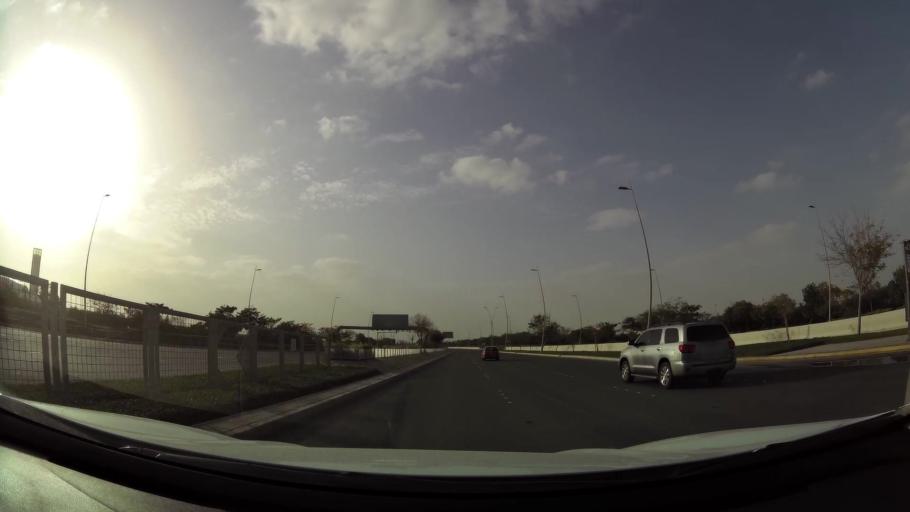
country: AE
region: Abu Dhabi
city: Abu Dhabi
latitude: 24.4965
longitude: 54.5899
